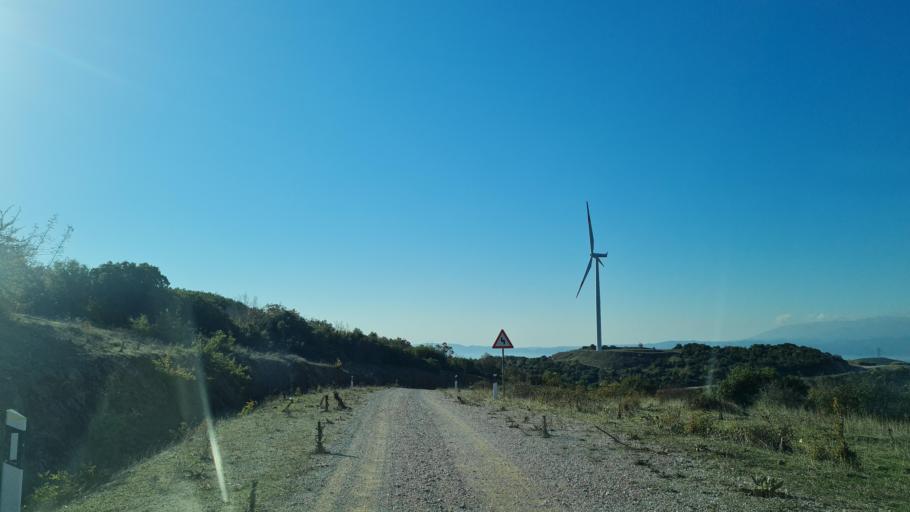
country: MK
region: Bogdanci
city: Bogdanci
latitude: 41.2212
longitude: 22.5479
